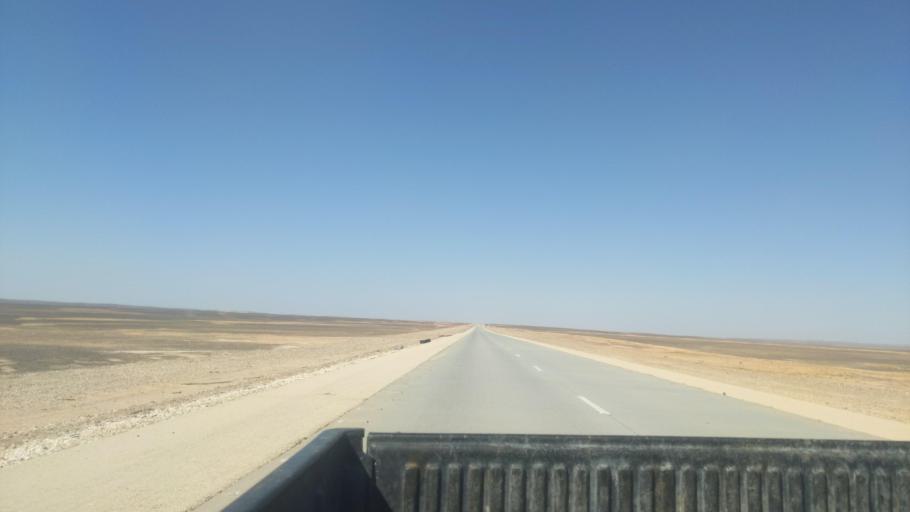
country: JO
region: Amman
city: Al Azraq ash Shamali
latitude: 31.4466
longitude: 36.7634
